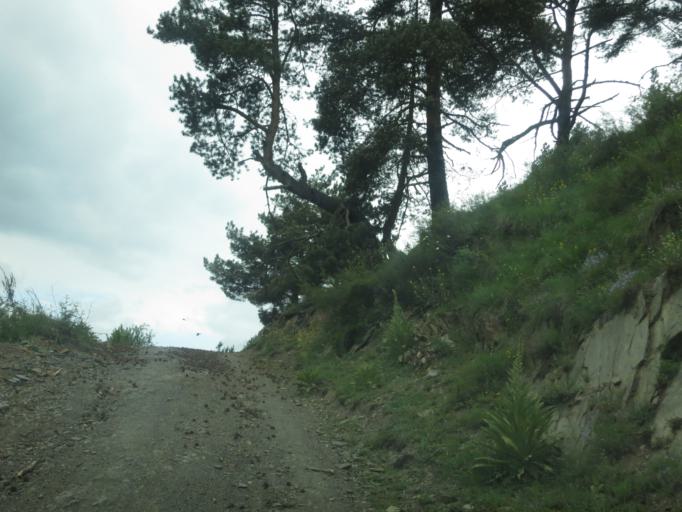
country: RU
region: Chechnya
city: Itum-Kali
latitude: 42.3670
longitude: 45.6536
